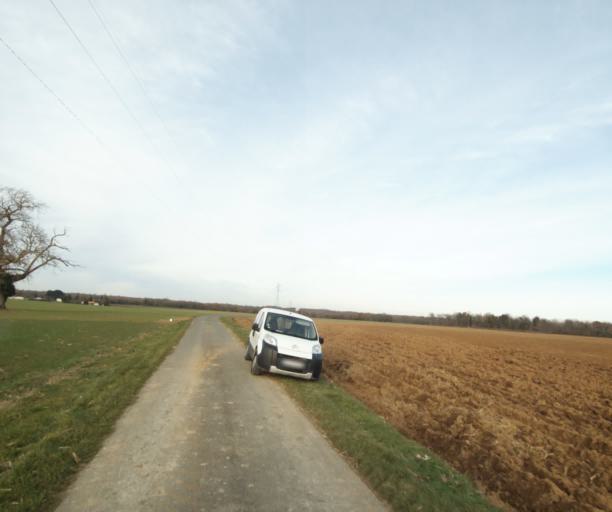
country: FR
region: Poitou-Charentes
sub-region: Departement de la Charente-Maritime
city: Saint-Hilaire-de-Villefranche
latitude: 45.8308
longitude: -0.5811
